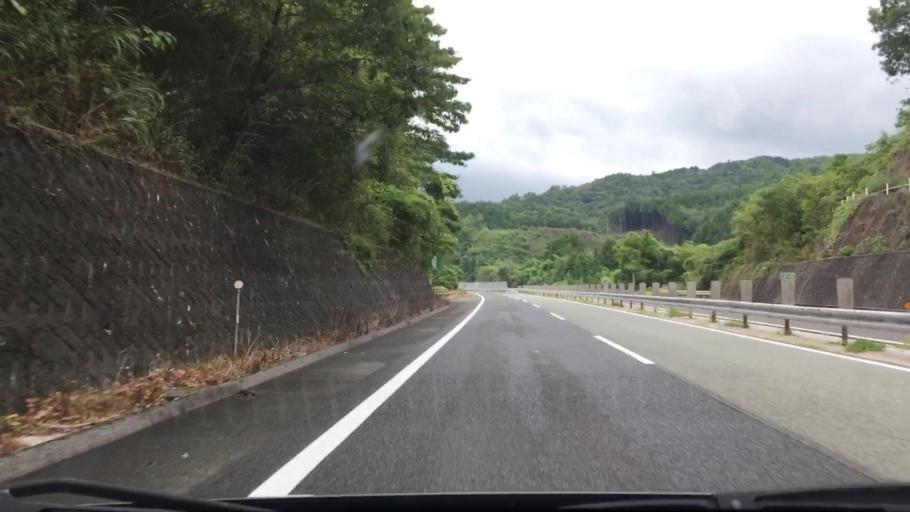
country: JP
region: Okayama
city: Niimi
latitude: 34.9429
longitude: 133.3289
